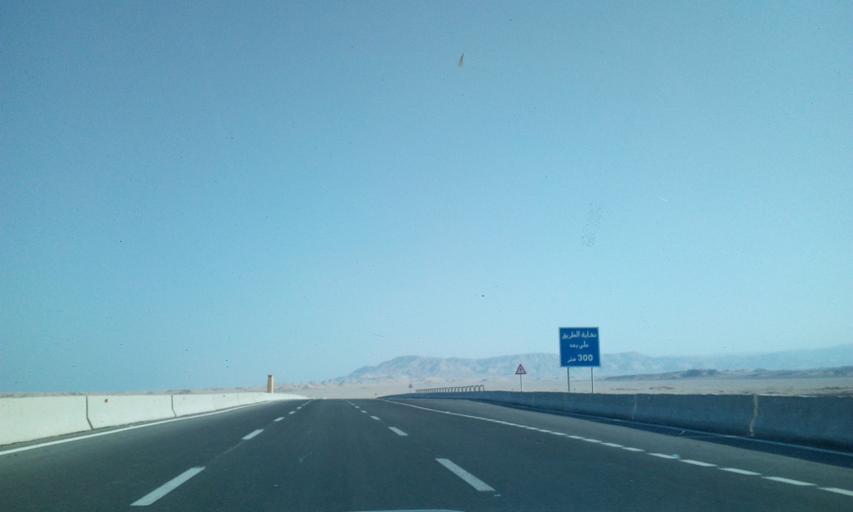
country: EG
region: As Suways
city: Ain Sukhna
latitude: 29.1098
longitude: 32.5329
